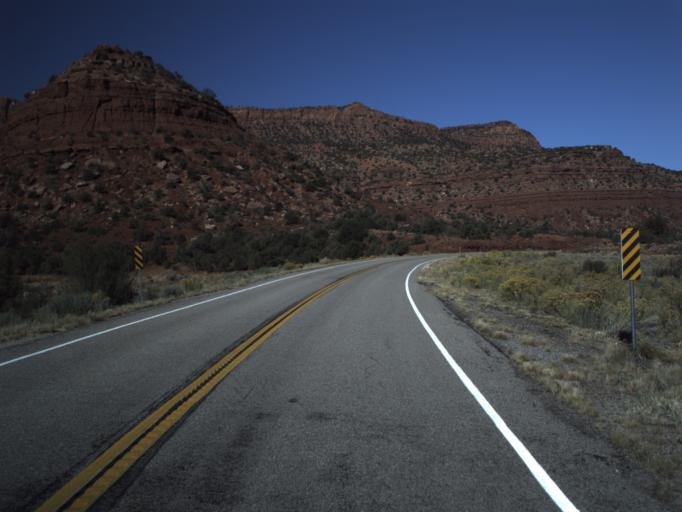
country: US
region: Utah
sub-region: San Juan County
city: Blanding
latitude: 37.6359
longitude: -110.1565
